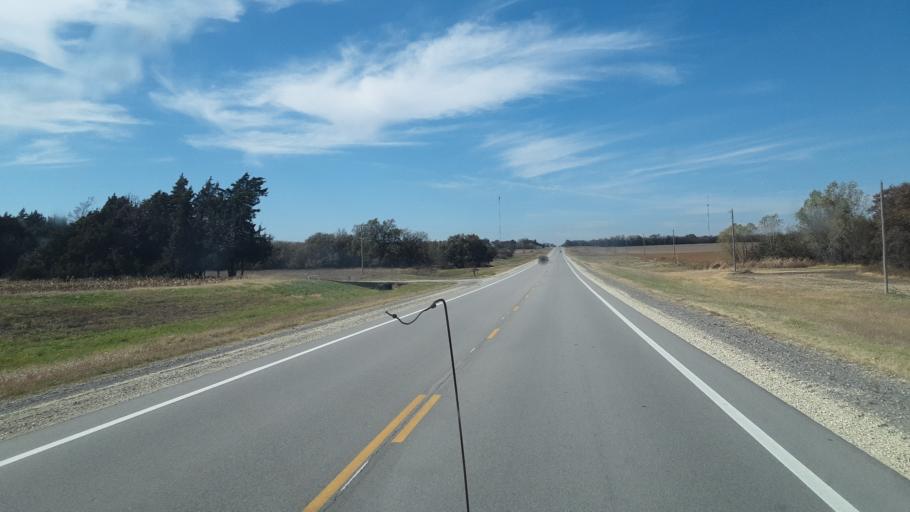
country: US
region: Kansas
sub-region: McPherson County
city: McPherson
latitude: 38.3760
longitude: -97.5831
